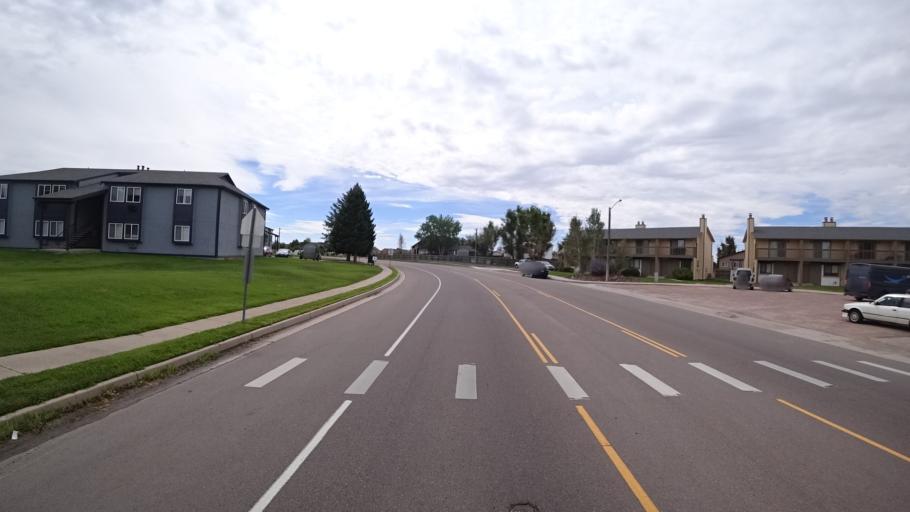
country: US
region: Colorado
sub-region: El Paso County
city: Fountain
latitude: 38.6964
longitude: -104.6991
